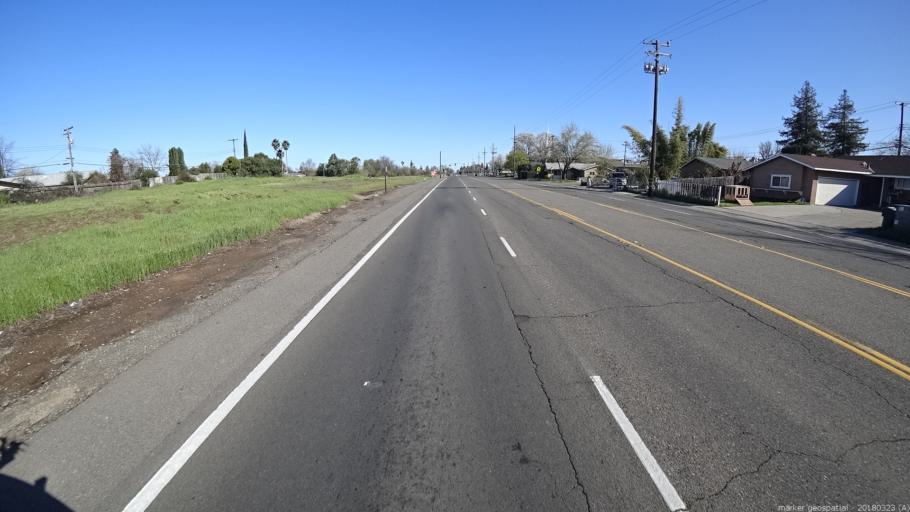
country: US
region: California
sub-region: Sacramento County
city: North Highlands
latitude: 38.6829
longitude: -121.3639
